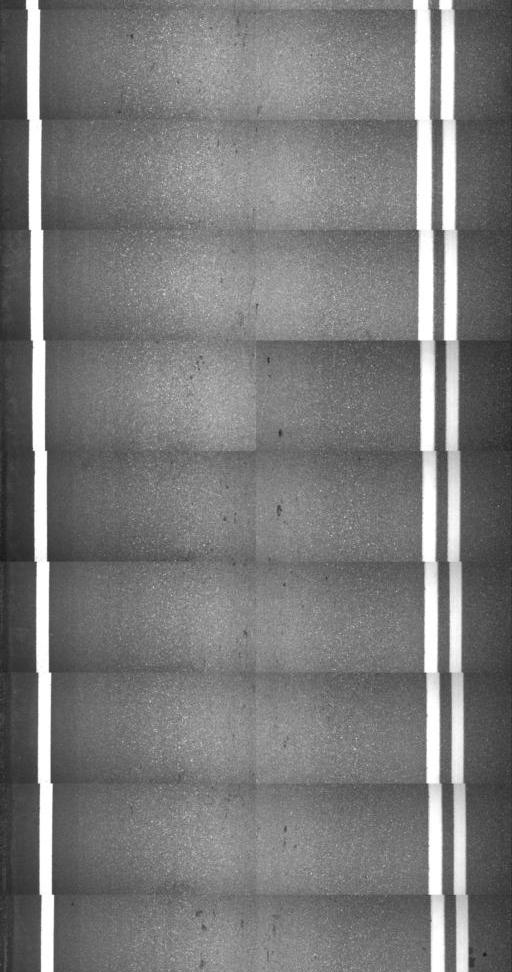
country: US
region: Vermont
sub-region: Windham County
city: Dover
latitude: 43.0919
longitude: -72.8678
